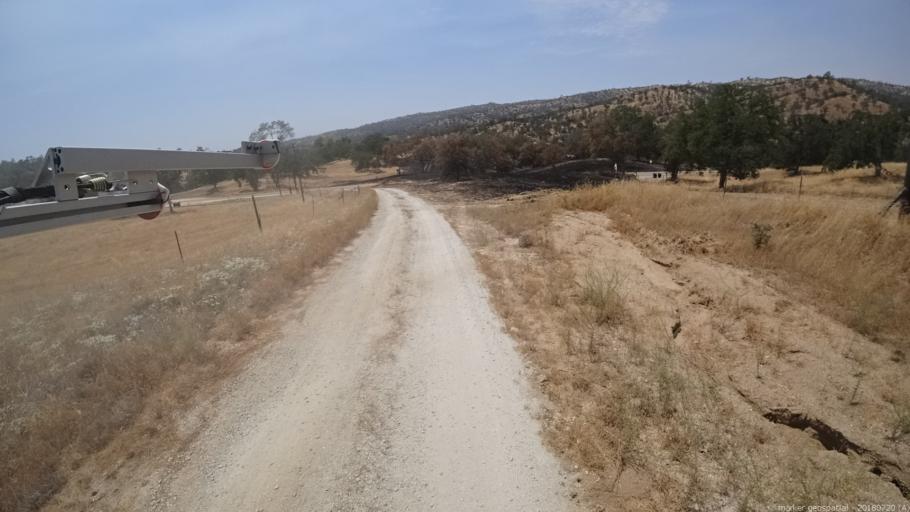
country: US
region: California
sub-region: Madera County
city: Yosemite Lakes
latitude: 37.1981
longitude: -119.7992
